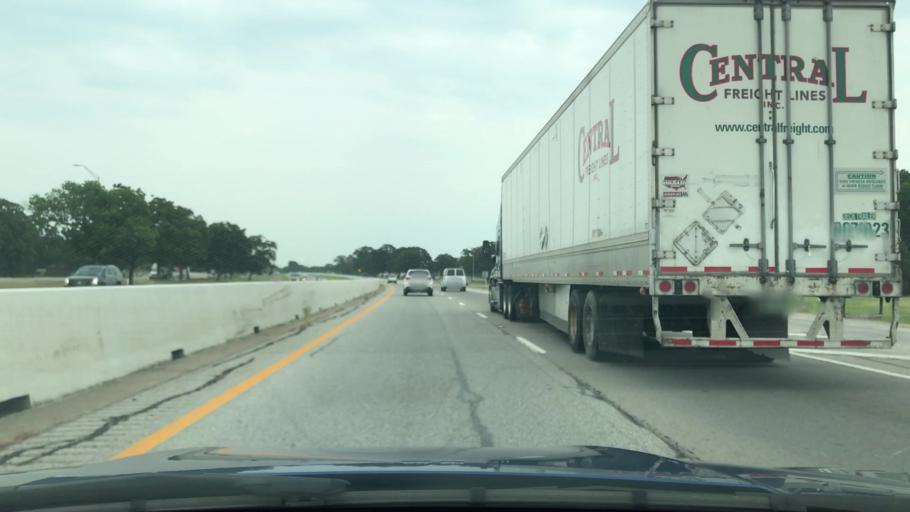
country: US
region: Texas
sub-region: Van Zandt County
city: Van
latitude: 32.5157
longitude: -95.6902
